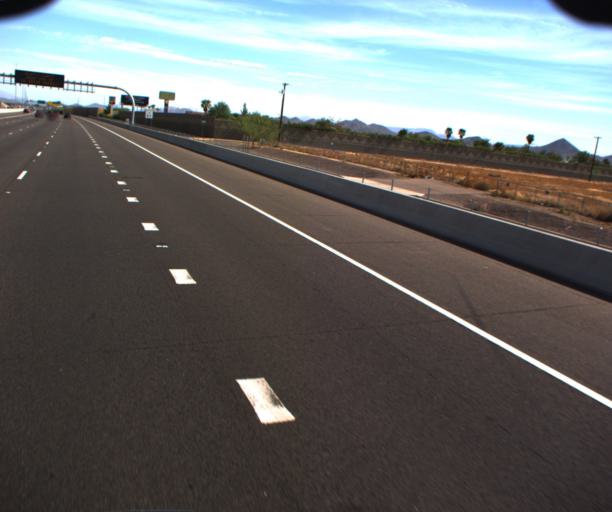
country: US
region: Arizona
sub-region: Maricopa County
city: Peoria
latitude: 33.6899
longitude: -112.1126
